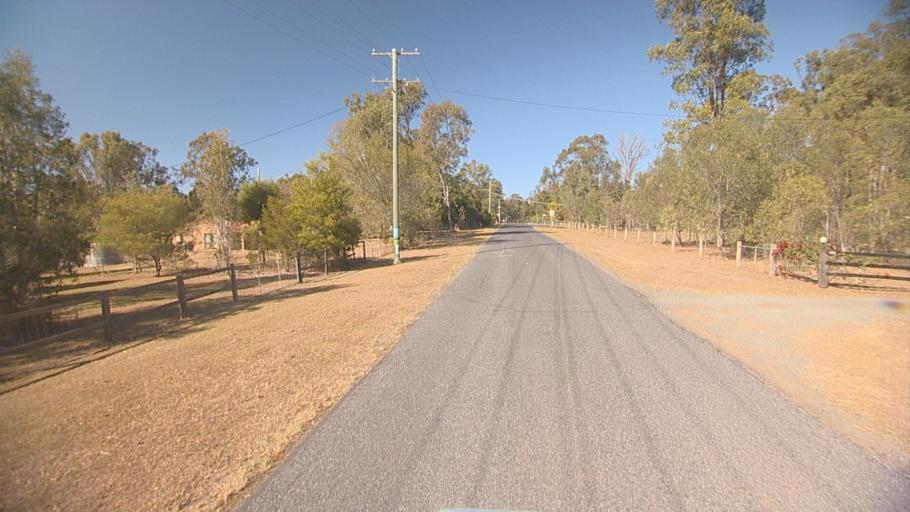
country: AU
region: Queensland
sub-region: Logan
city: Cedar Vale
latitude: -27.8726
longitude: 152.9840
